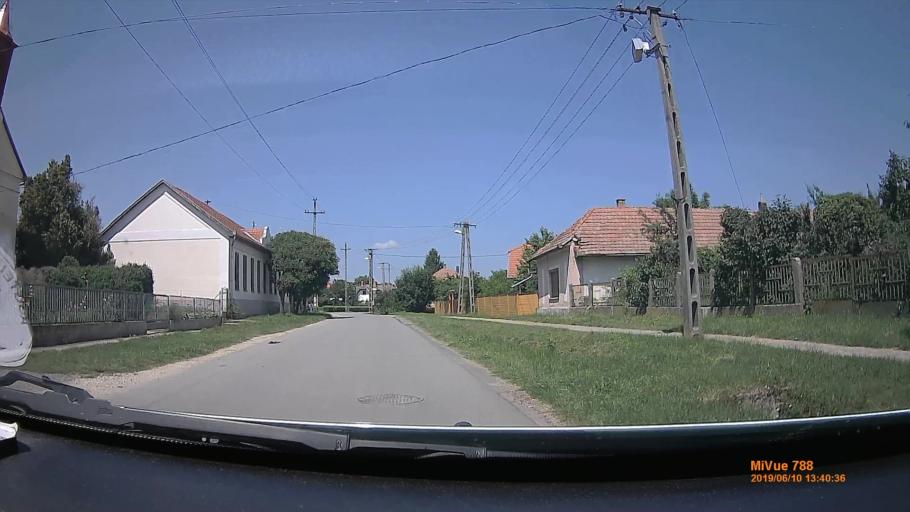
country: HU
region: Szabolcs-Szatmar-Bereg
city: Tiszadob
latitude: 48.0112
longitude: 21.1674
